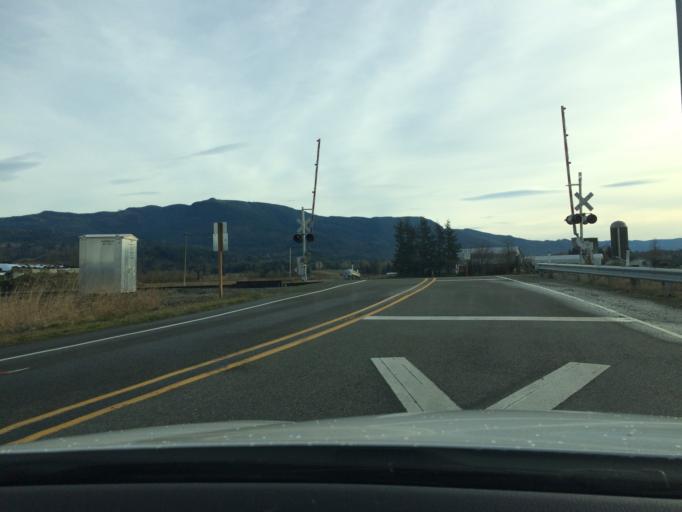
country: US
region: Washington
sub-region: Whatcom County
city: Sumas
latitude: 48.9638
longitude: -122.2885
